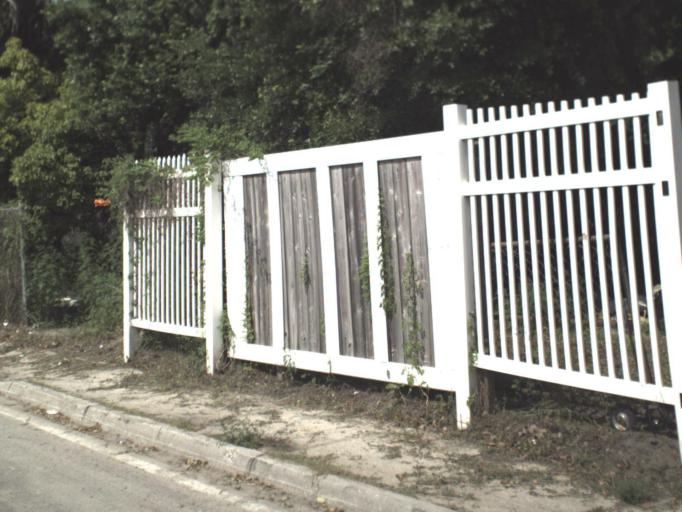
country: US
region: Florida
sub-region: Duval County
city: Jacksonville
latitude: 30.3551
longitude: -81.6411
